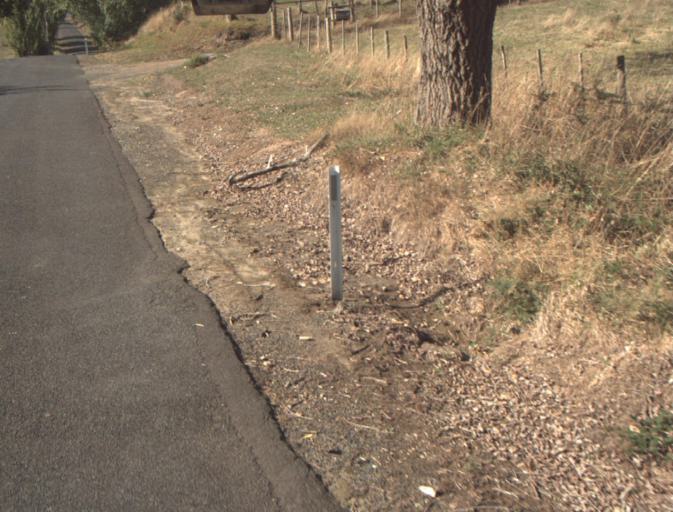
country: AU
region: Tasmania
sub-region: Launceston
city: Mayfield
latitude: -41.2888
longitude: 147.2096
